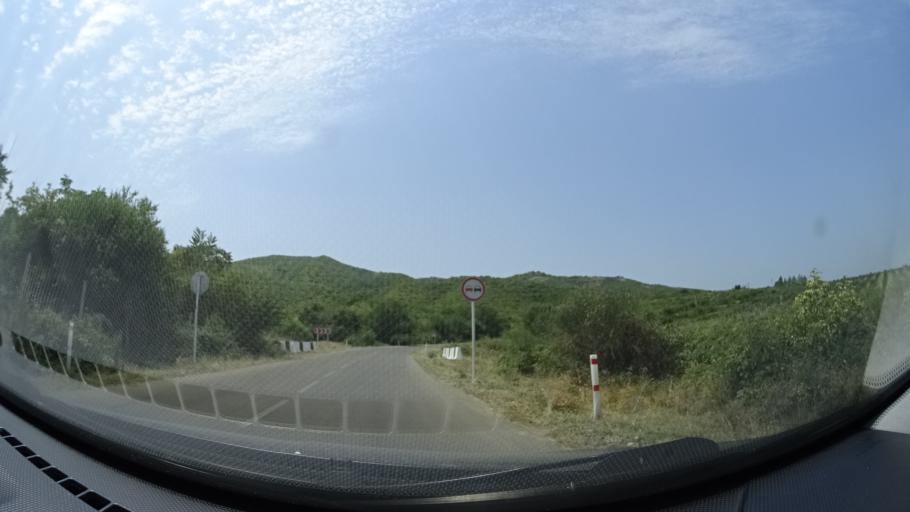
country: GE
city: Tsnori
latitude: 41.6214
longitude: 45.9463
